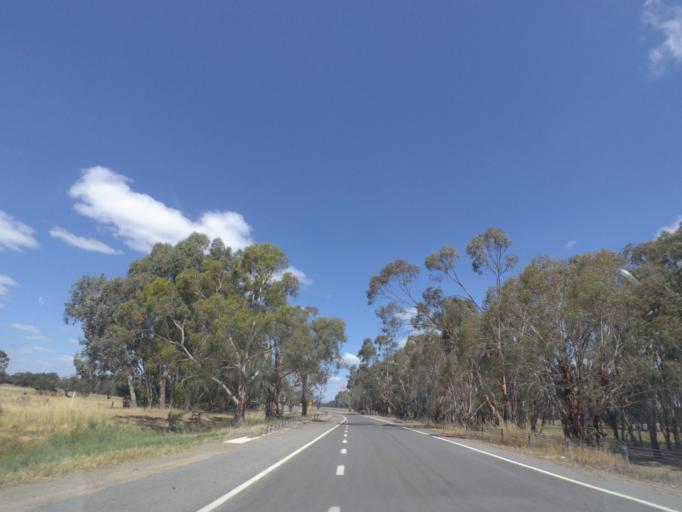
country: AU
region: Victoria
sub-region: Wangaratta
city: Wangaratta
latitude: -36.4025
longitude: 146.2991
